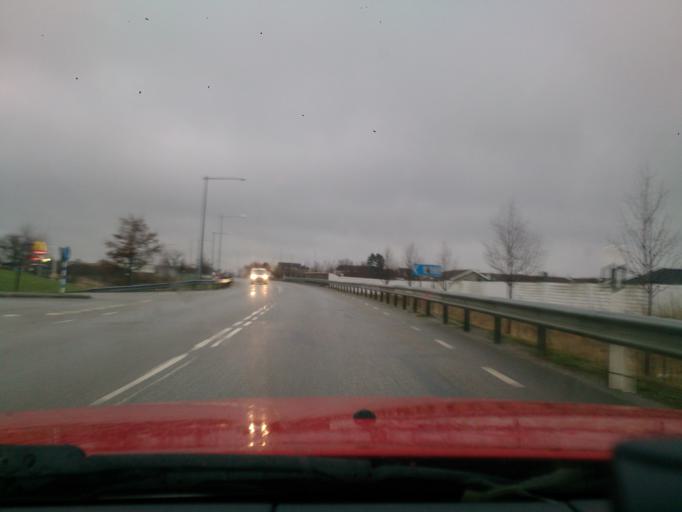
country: SE
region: Skane
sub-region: Ystads Kommun
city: Ystad
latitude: 55.4365
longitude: 13.7898
